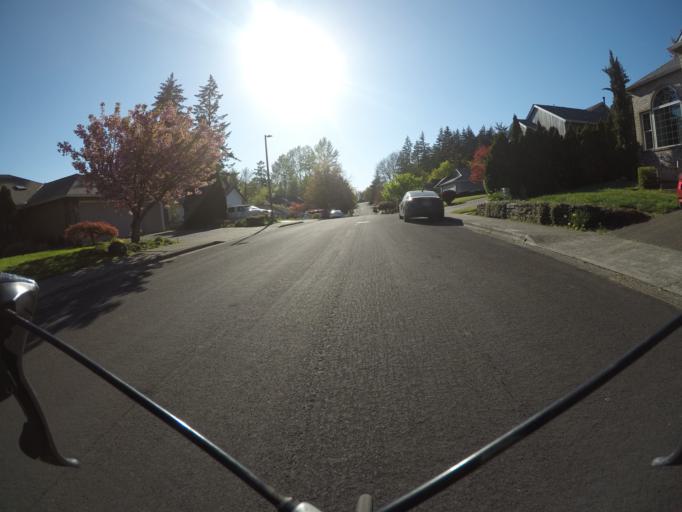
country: US
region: Oregon
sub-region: Washington County
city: King City
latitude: 45.4071
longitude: -122.8283
